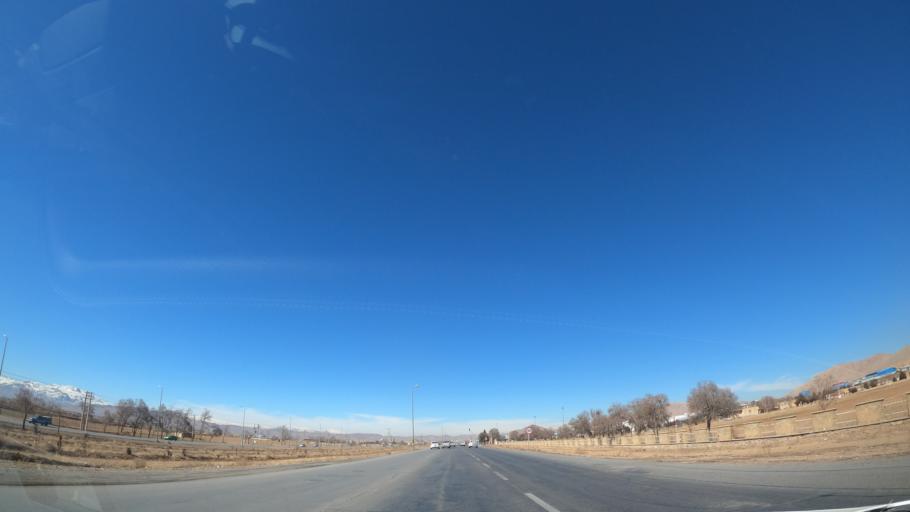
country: IR
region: Chahar Mahall va Bakhtiari
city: Farrokh Shahr
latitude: 32.2965
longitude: 50.9319
